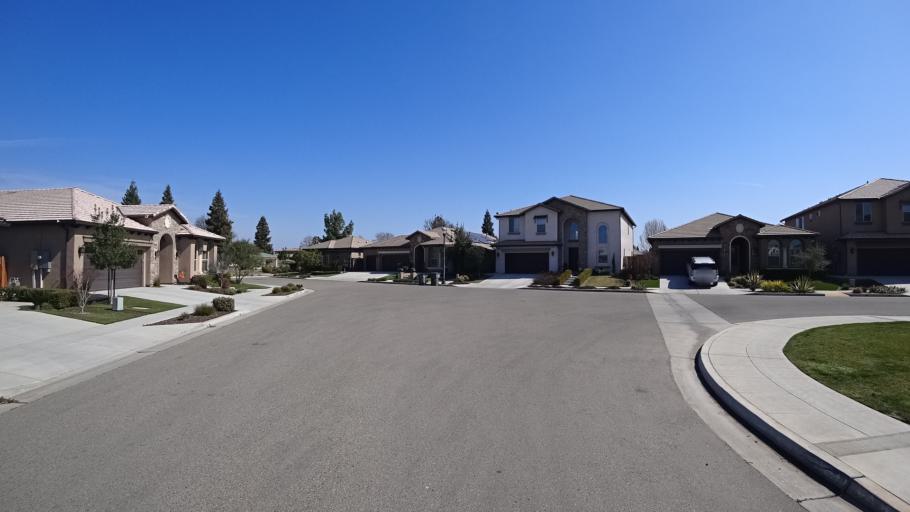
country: US
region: California
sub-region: Fresno County
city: Clovis
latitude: 36.8999
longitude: -119.7488
